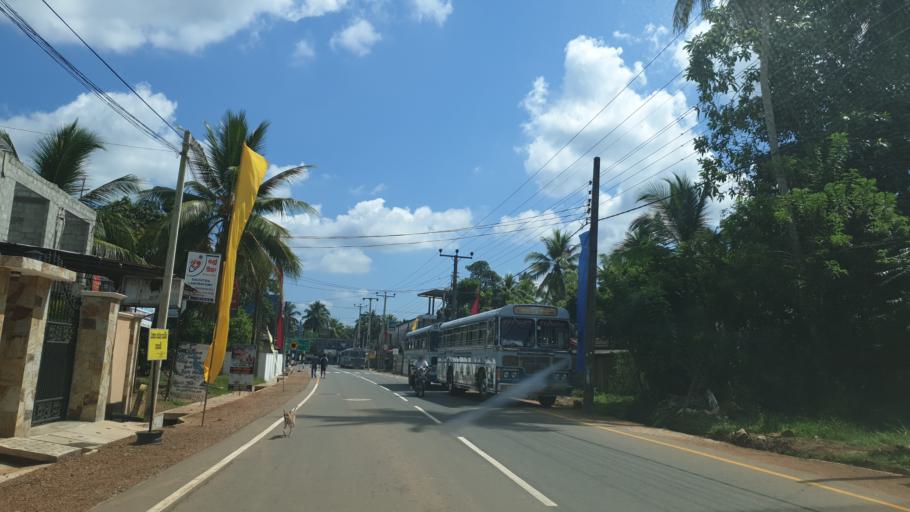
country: LK
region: Western
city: Kalutara
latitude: 6.6634
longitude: 79.9704
